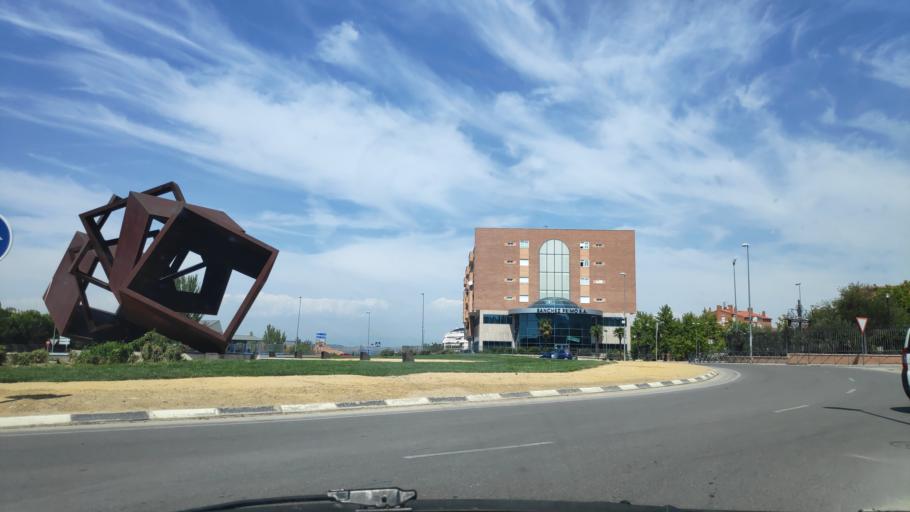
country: ES
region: Madrid
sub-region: Provincia de Madrid
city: Arganda
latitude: 40.3063
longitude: -3.4472
